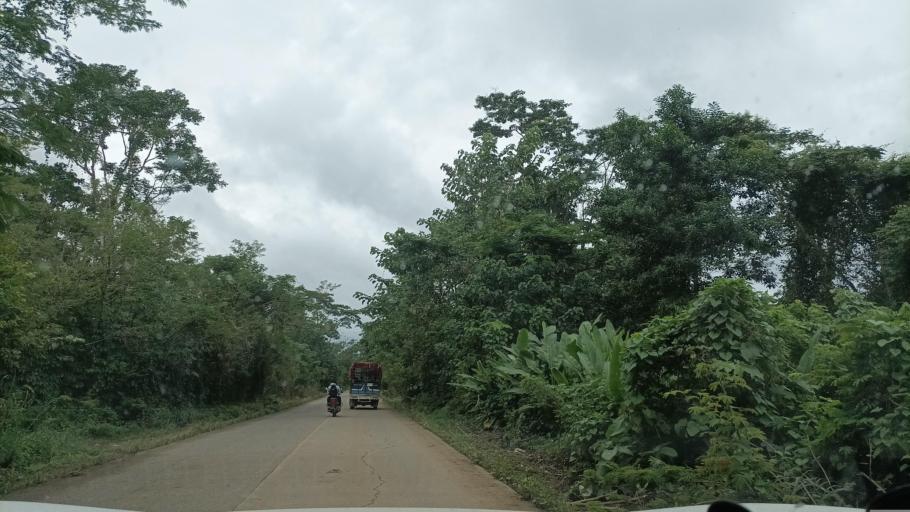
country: MX
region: Veracruz
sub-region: Uxpanapa
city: Poblado 10
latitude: 17.2786
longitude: -94.4791
